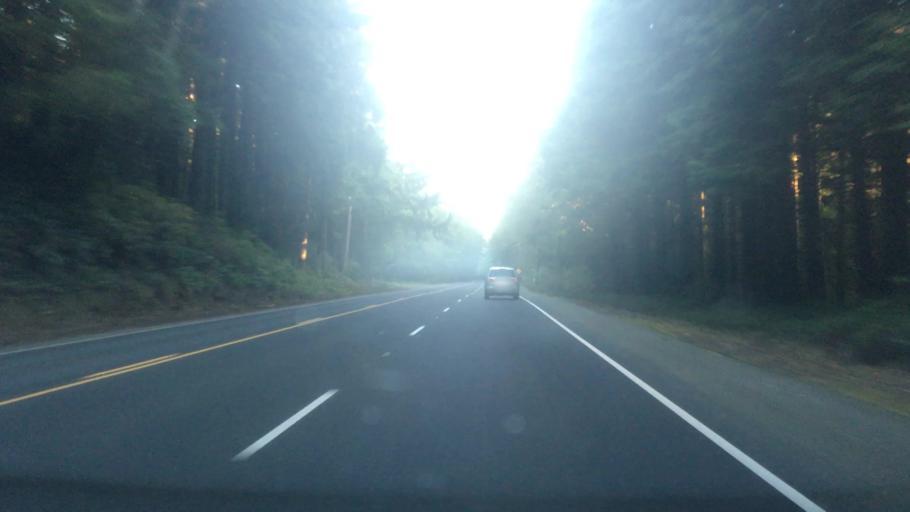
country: US
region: Oregon
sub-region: Clatsop County
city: Cannon Beach
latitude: 45.7899
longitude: -123.9599
